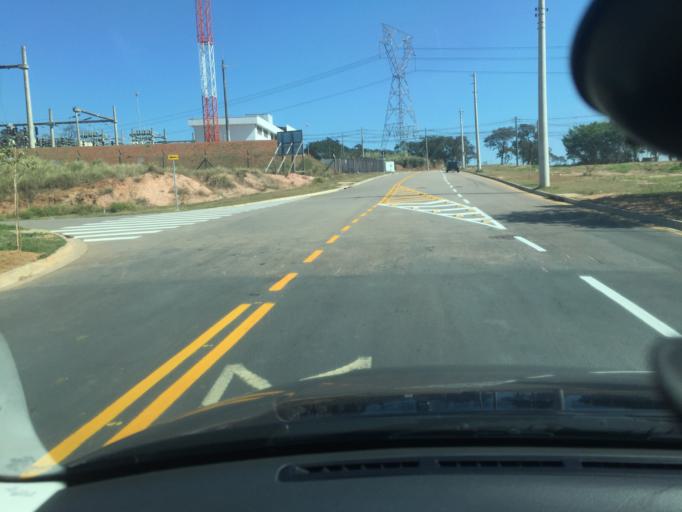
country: BR
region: Sao Paulo
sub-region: Itupeva
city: Itupeva
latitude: -23.1473
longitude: -46.9978
